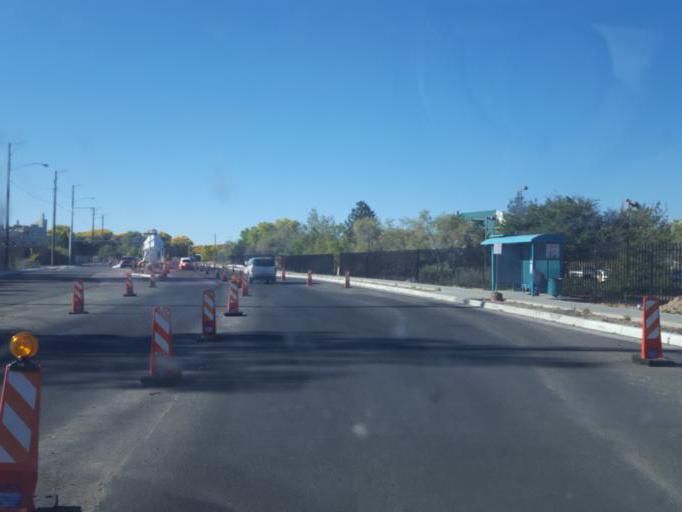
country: US
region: New Mexico
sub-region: Bernalillo County
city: Albuquerque
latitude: 35.0943
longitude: -106.6777
